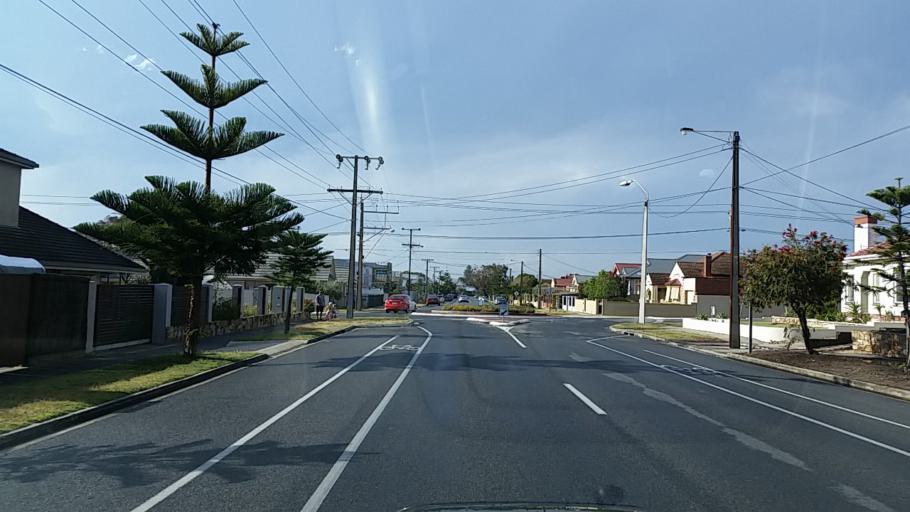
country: AU
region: South Australia
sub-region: Charles Sturt
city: Henley Beach
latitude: -34.9110
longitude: 138.4966
